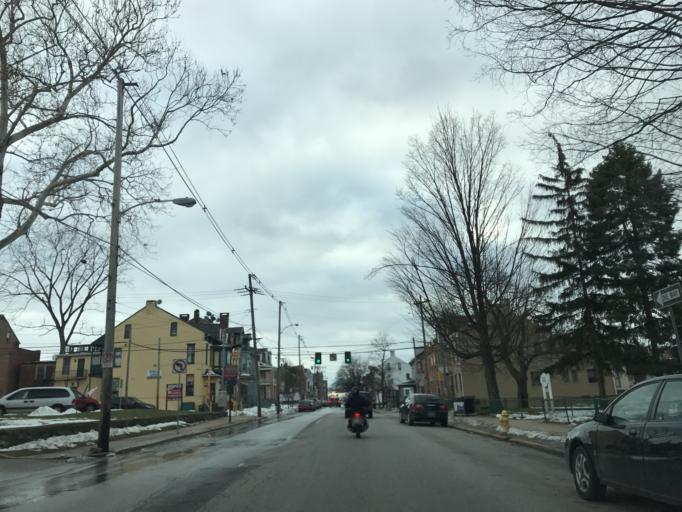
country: US
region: Pennsylvania
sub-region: York County
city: York
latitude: 39.9659
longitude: -76.7218
